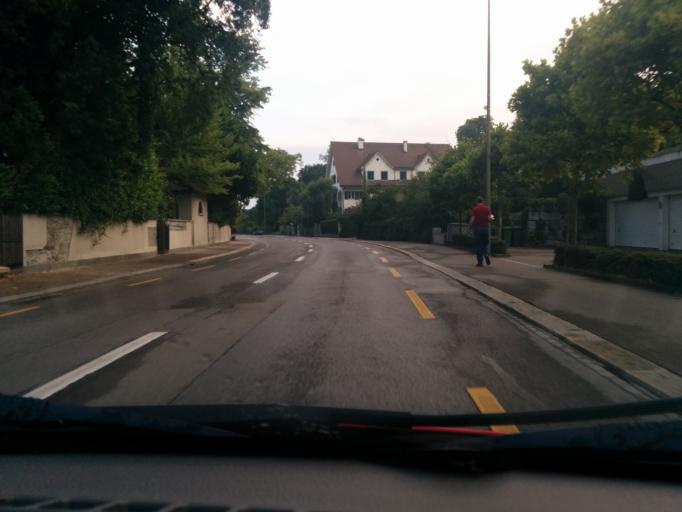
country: CH
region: Zurich
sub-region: Bezirk Meilen
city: Kuesnacht / Goldbach
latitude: 47.3292
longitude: 8.5732
